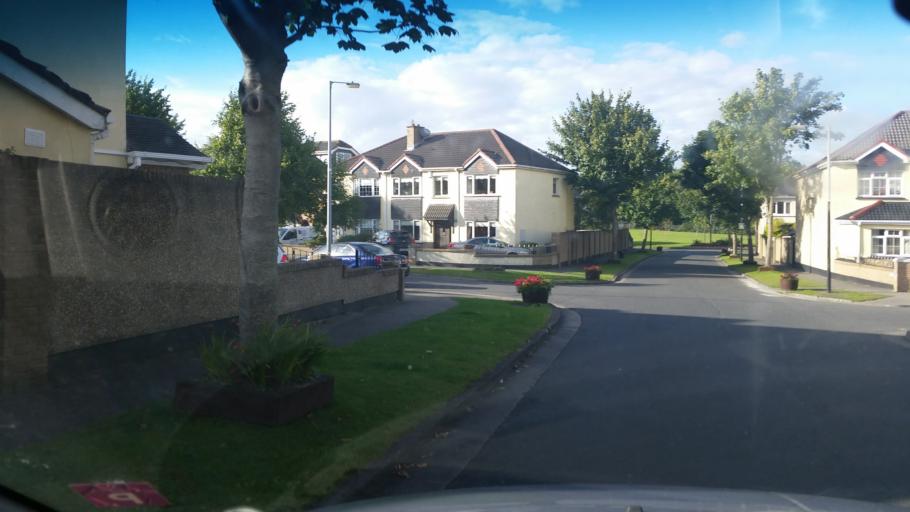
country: IE
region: Leinster
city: Beaumont
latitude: 53.4006
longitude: -6.2310
